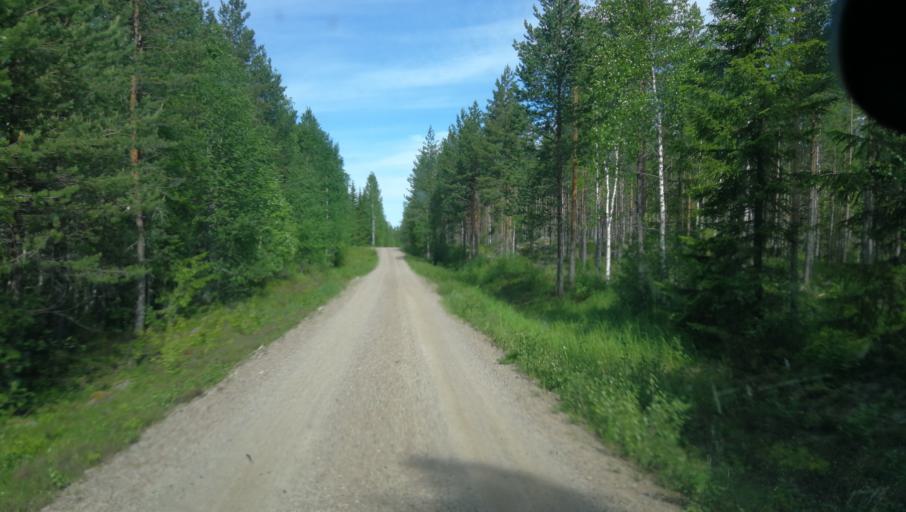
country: SE
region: Dalarna
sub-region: Vansbro Kommun
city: Vansbro
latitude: 60.8266
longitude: 14.1668
